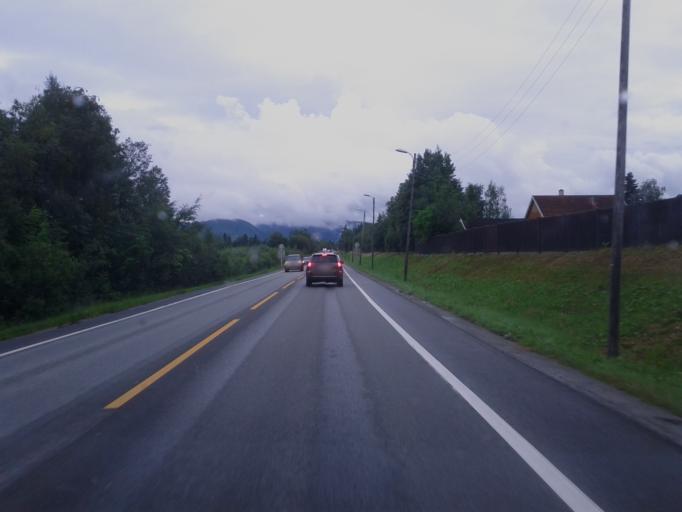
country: NO
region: Sor-Trondelag
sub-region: Trondheim
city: Trondheim
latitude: 63.3528
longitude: 10.3699
